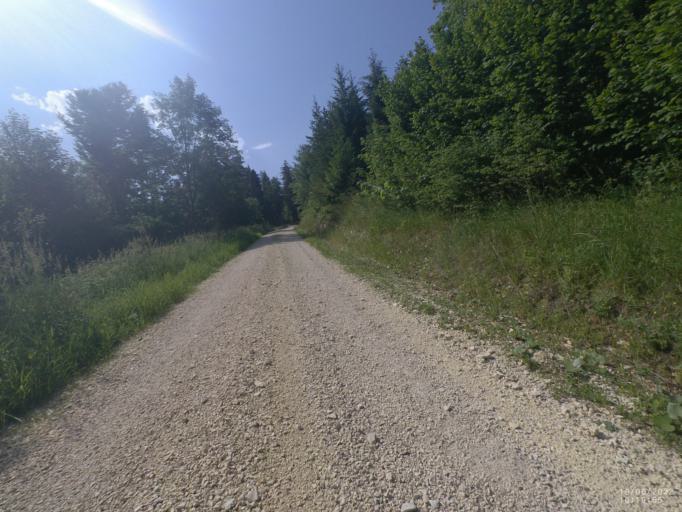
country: DE
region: Baden-Wuerttemberg
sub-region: Regierungsbezirk Stuttgart
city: Gerstetten
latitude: 48.6063
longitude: 9.9987
